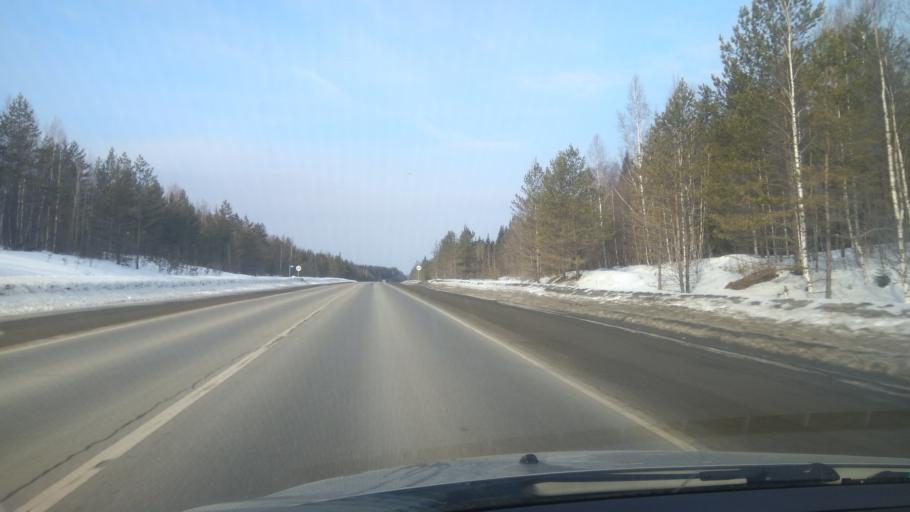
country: RU
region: Sverdlovsk
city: Nizhniye Sergi
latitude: 56.8251
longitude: 59.2446
